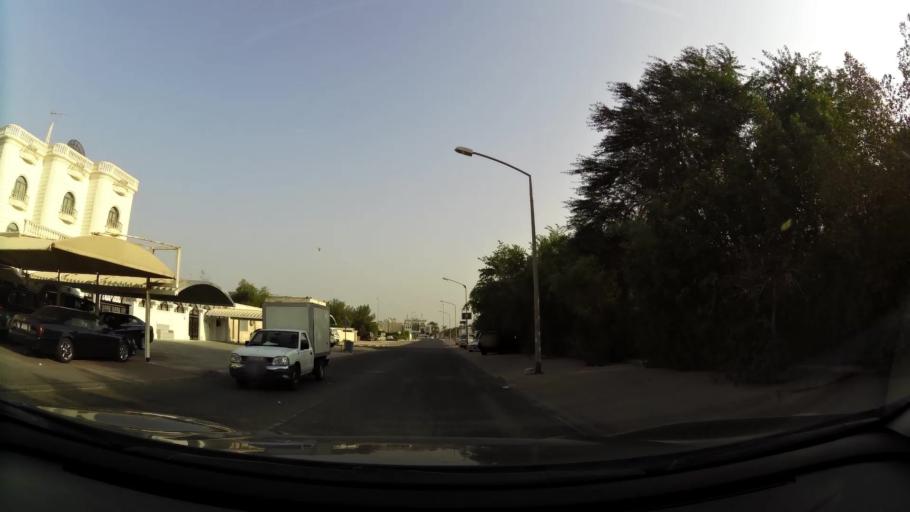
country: KW
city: Bayan
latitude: 29.3070
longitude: 48.0596
